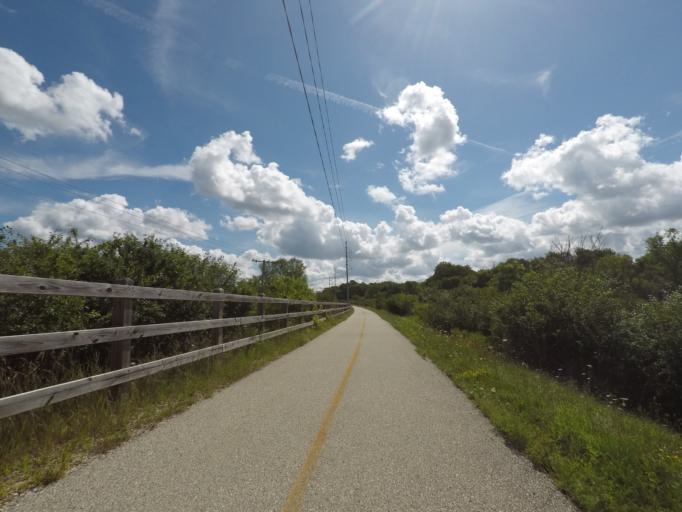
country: US
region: Wisconsin
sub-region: Waukesha County
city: Hartland
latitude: 43.0573
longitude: -88.3486
